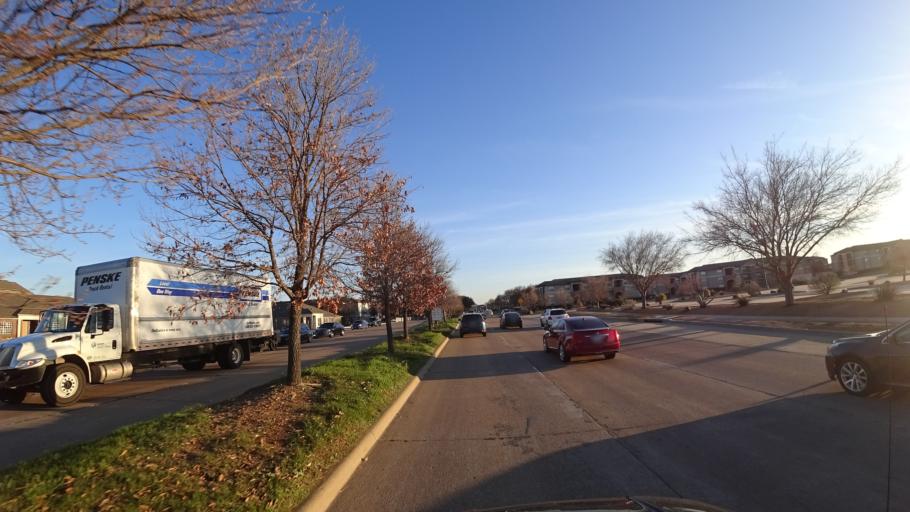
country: US
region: Texas
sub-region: Denton County
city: Lewisville
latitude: 32.9983
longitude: -96.9763
